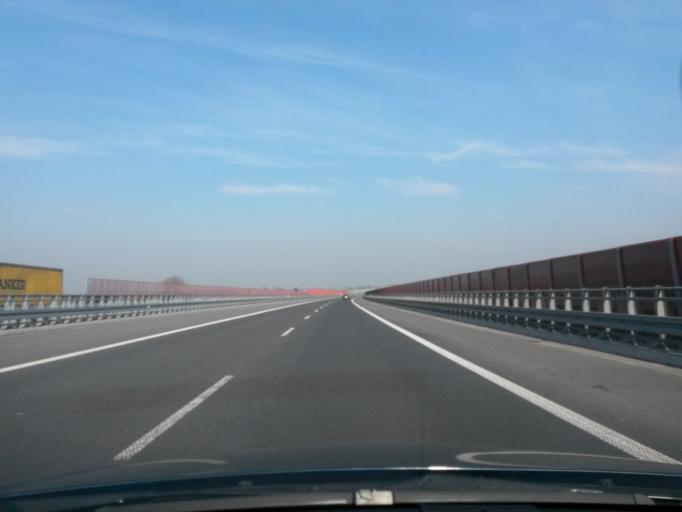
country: PL
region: Lodz Voivodeship
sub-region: Powiat kutnowski
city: Krzyzanow
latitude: 52.1367
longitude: 19.4855
